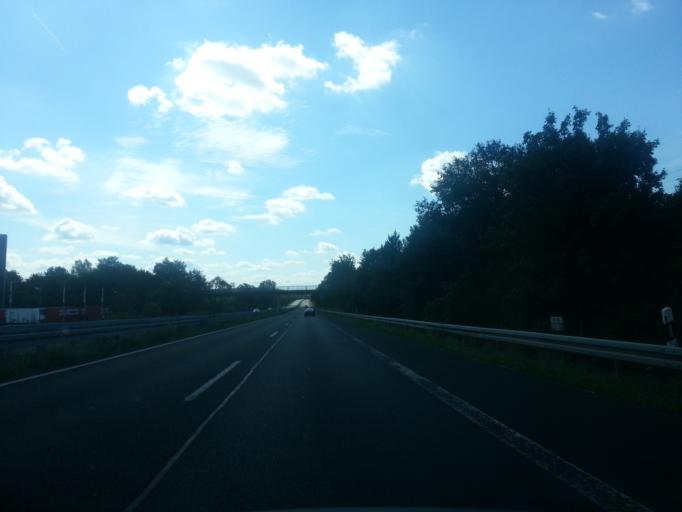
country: DE
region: Hesse
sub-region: Regierungsbezirk Darmstadt
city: Eppertshausen
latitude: 49.9466
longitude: 8.8327
